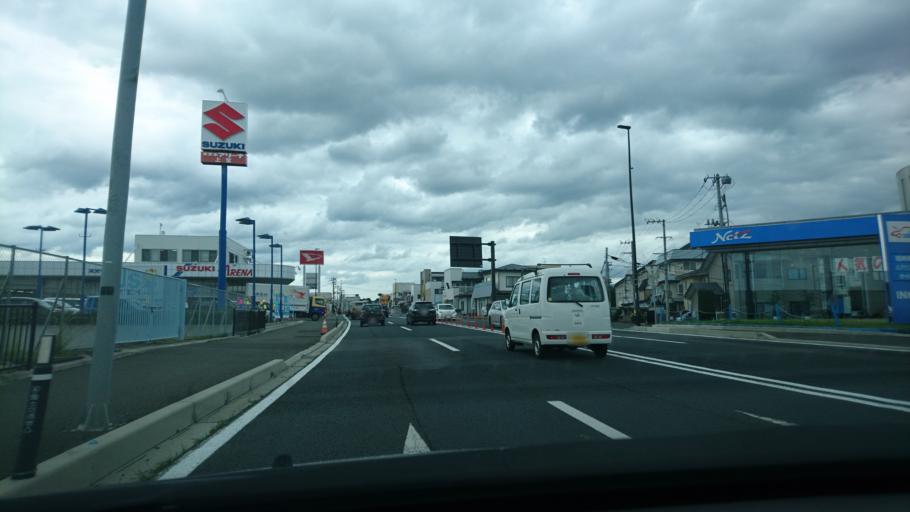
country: JP
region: Iwate
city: Morioka-shi
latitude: 39.7401
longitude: 141.1276
